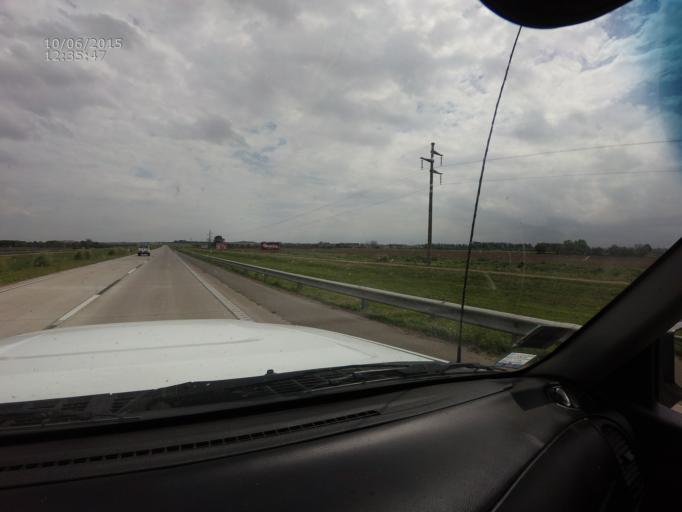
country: AR
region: Santa Fe
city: Carcarana
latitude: -32.8737
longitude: -61.1837
